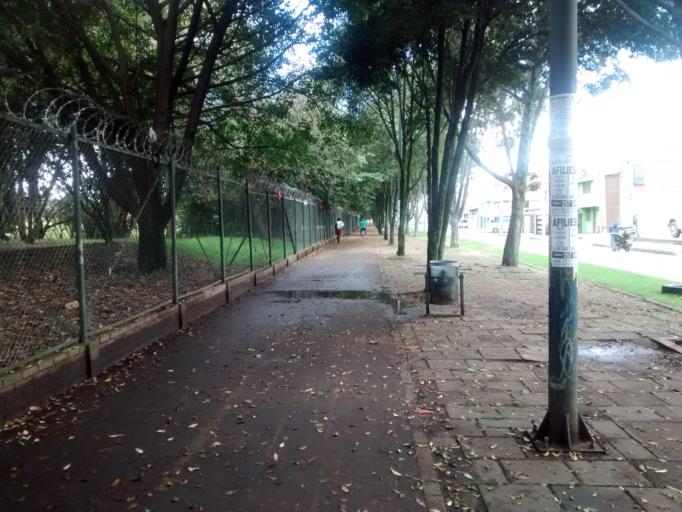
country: CO
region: Bogota D.C.
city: Barrio San Luis
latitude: 4.6965
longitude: -74.0942
